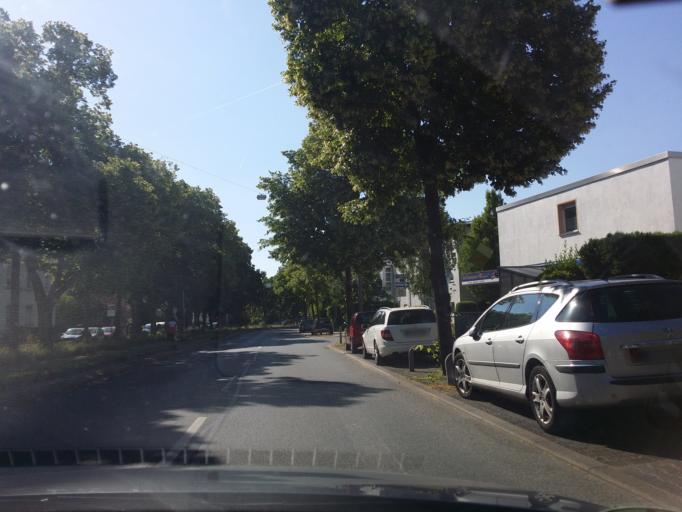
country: DE
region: Hesse
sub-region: Regierungsbezirk Darmstadt
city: Wiesbaden
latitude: 50.0925
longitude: 8.2259
